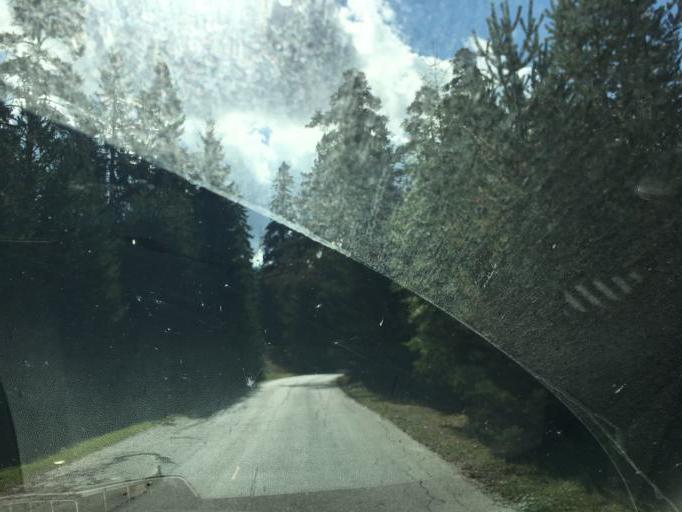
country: BG
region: Pazardzhik
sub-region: Obshtina Batak
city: Batak
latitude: 41.9268
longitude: 24.2786
